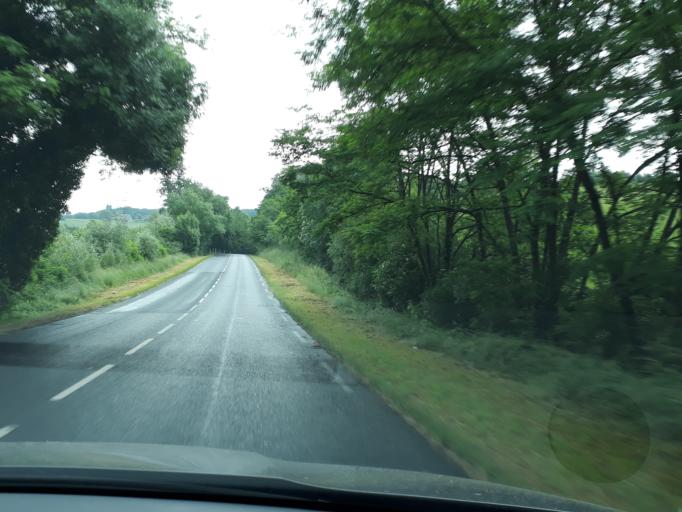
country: FR
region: Limousin
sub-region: Departement de la Correze
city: Malemort-sur-Correze
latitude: 45.1635
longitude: 1.5854
